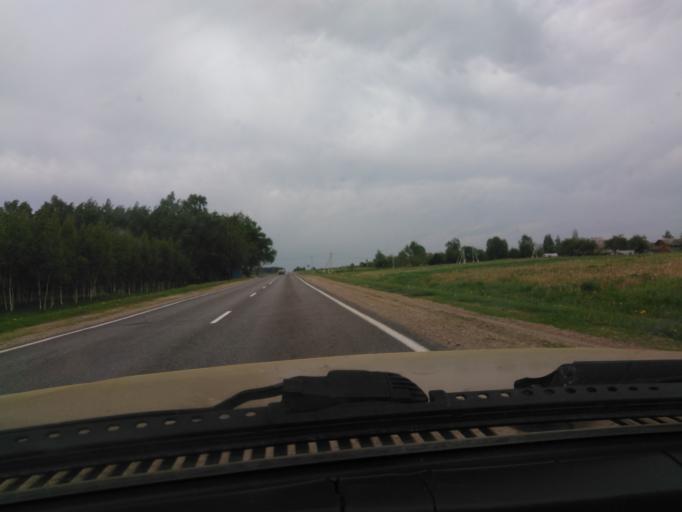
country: BY
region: Mogilev
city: Palykavichy Pyershyya
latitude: 54.0332
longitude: 30.3238
